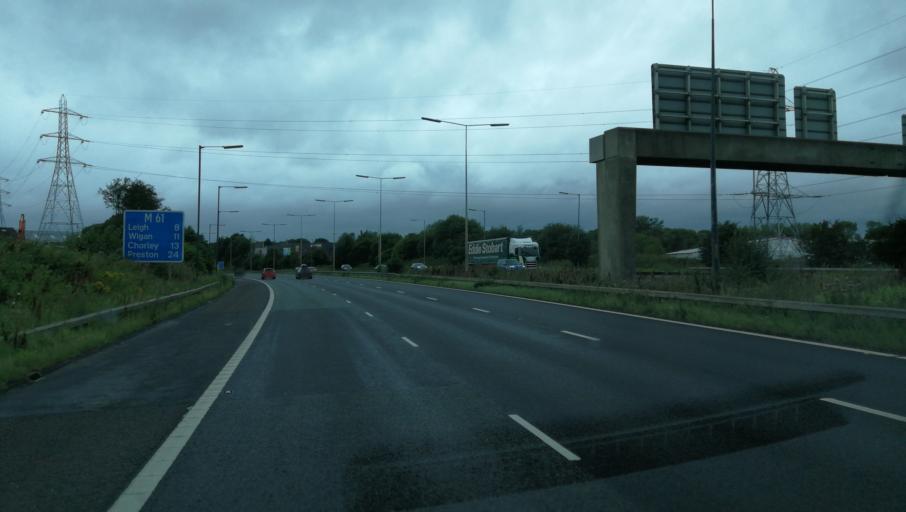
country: GB
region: England
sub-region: Borough of Bolton
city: Kearsley
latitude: 53.5372
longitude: -2.3947
